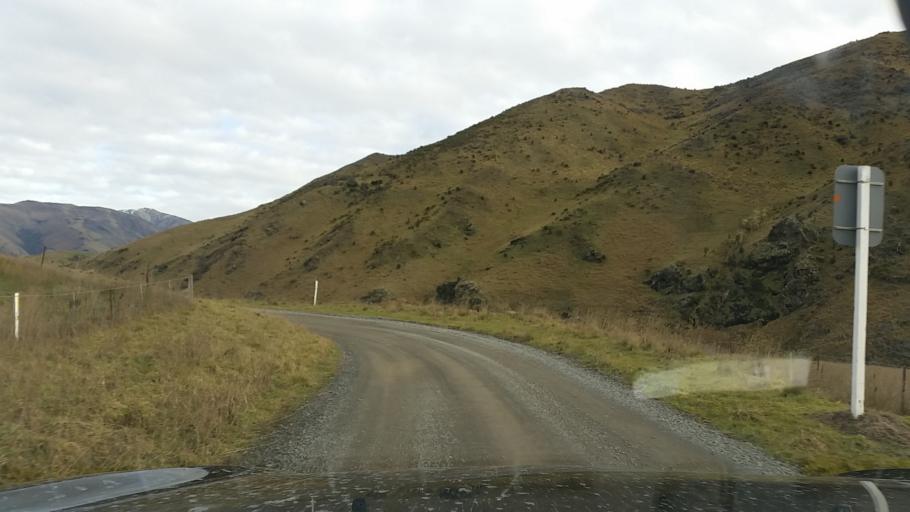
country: NZ
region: Marlborough
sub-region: Marlborough District
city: Blenheim
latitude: -41.8851
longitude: 173.6394
